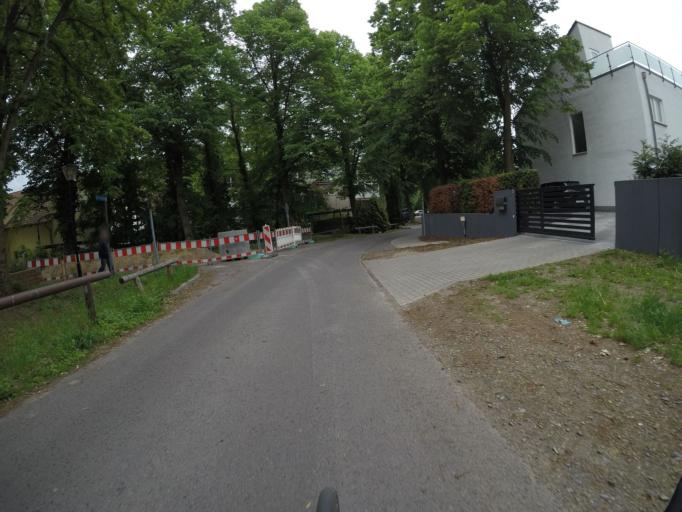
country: DE
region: Brandenburg
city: Glienicke
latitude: 52.6307
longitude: 13.3281
